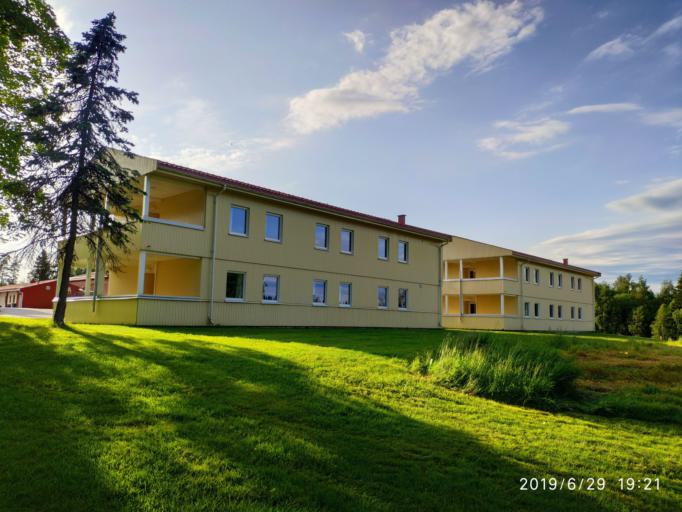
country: NO
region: Akershus
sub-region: Ullensaker
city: Jessheim
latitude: 60.1596
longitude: 11.1704
